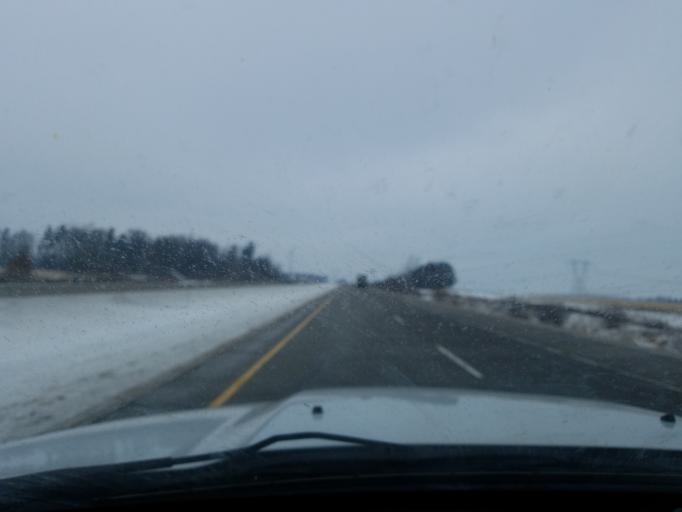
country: US
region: Indiana
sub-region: Marshall County
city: Argos
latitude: 41.1957
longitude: -86.2539
